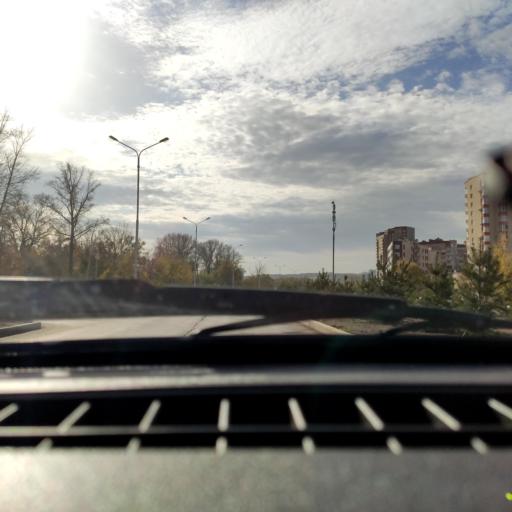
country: RU
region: Bashkortostan
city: Ufa
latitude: 54.7629
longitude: 56.0745
